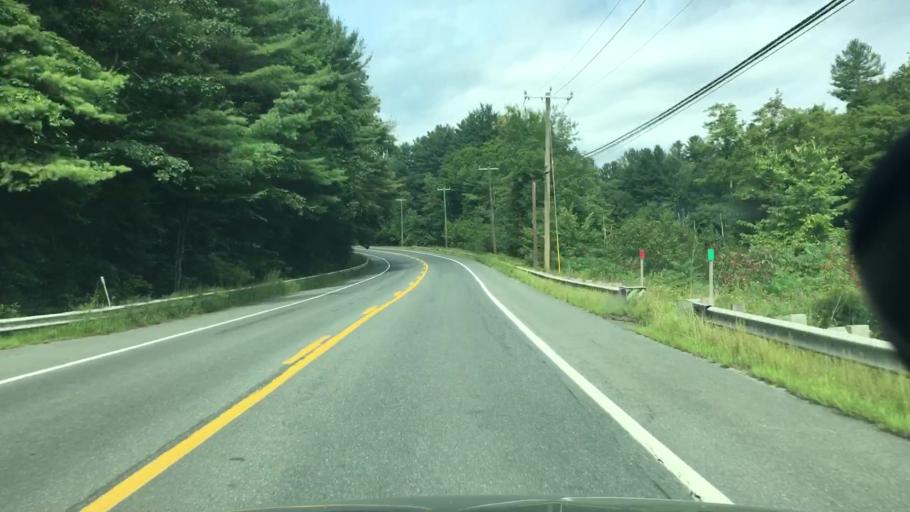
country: US
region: Massachusetts
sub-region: Franklin County
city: Shelburne
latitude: 42.6113
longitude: -72.6604
